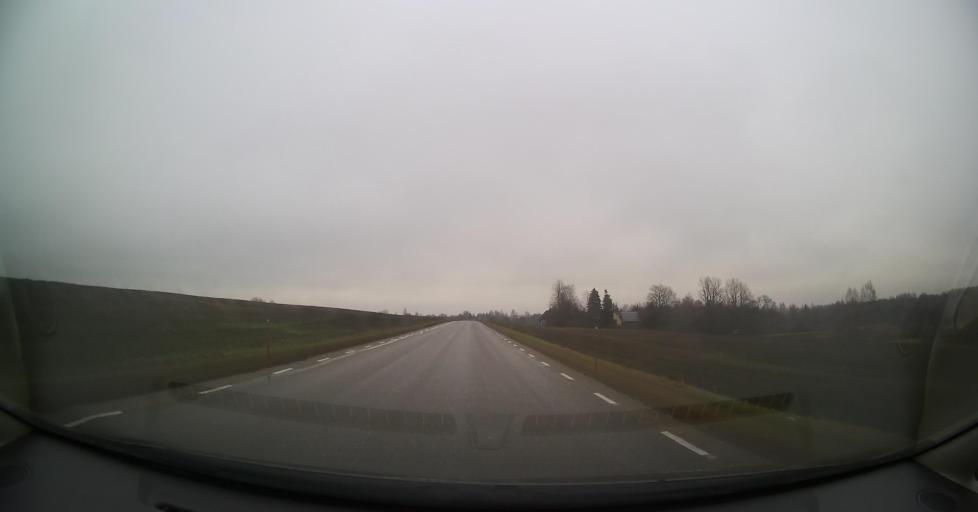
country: EE
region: Tartu
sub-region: Tartu linn
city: Tartu
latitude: 58.3828
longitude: 26.9781
